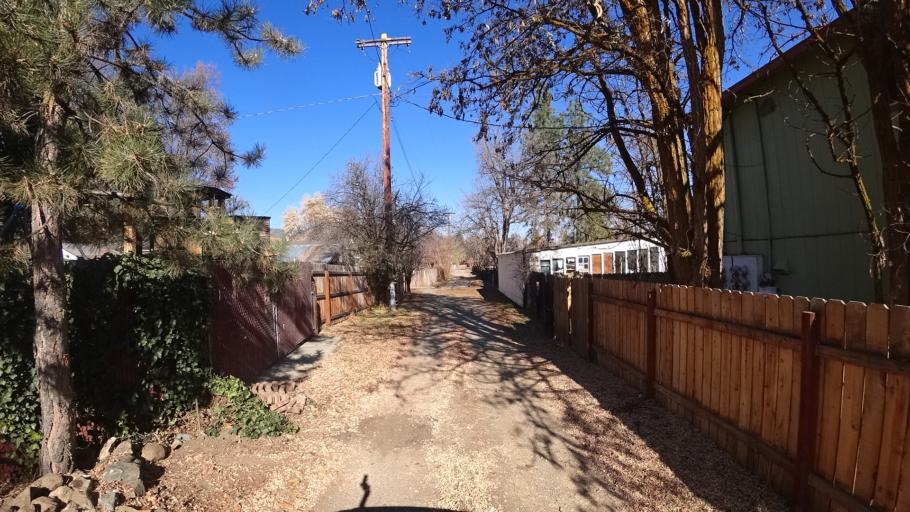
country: US
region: California
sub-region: Siskiyou County
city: Yreka
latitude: 41.7343
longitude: -122.6368
